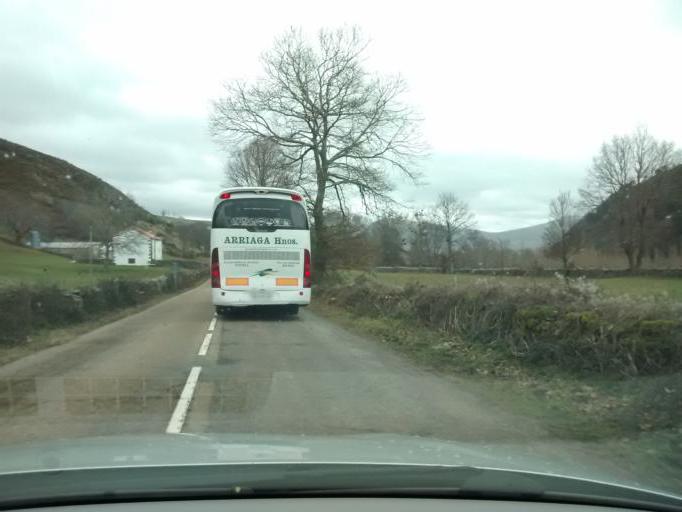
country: ES
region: Castille and Leon
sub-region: Provincia de Burgos
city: Espinosa de los Monteros
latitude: 43.0938
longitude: -3.5623
